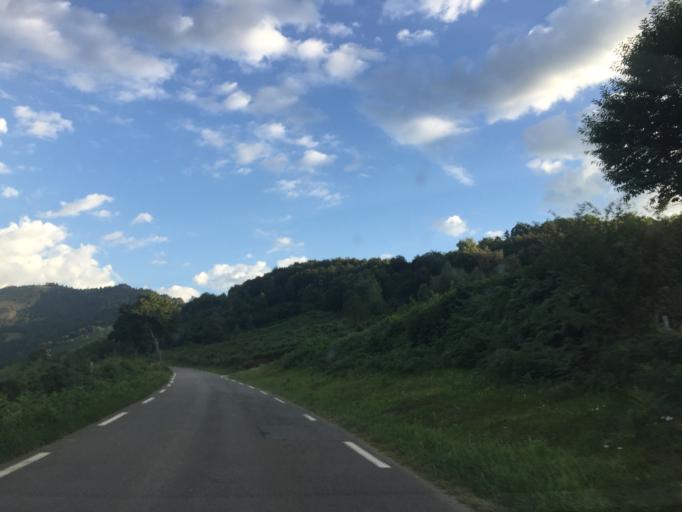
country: FR
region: Midi-Pyrenees
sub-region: Departement des Hautes-Pyrenees
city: Saint-Lary-Soulan
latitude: 42.9281
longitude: 0.3511
